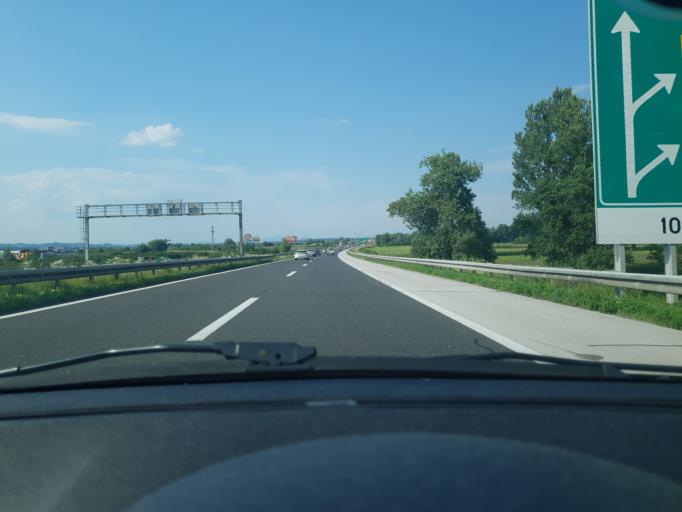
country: HR
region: Zagrebacka
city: Zapresic
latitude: 45.8415
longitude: 15.8207
